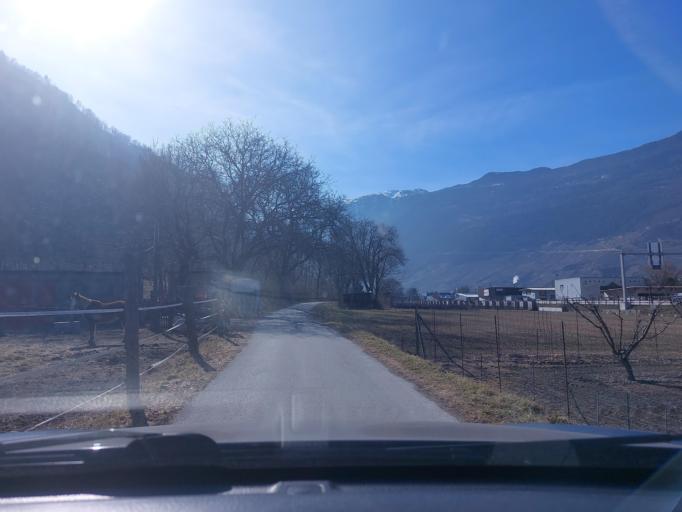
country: CH
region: Valais
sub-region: Martigny District
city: Martigny-Ville
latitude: 46.1000
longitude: 7.0904
